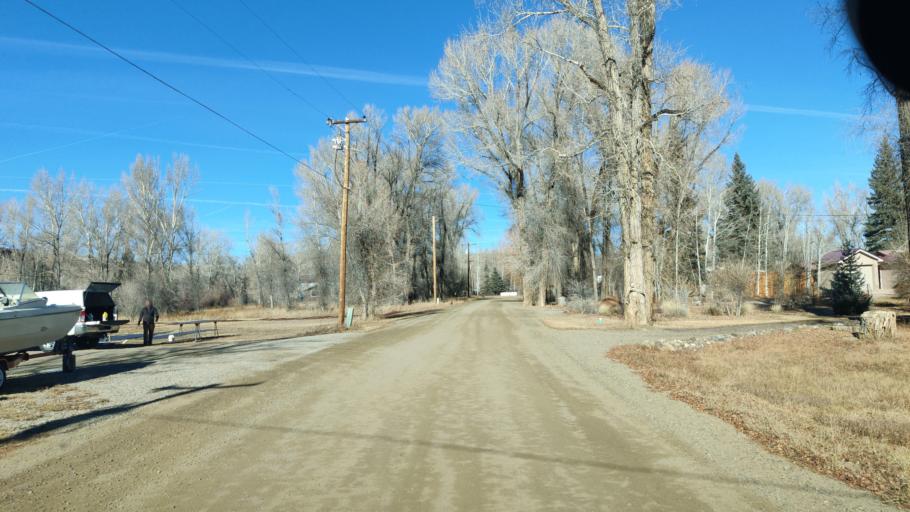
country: US
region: Colorado
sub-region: Gunnison County
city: Gunnison
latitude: 38.5357
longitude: -106.9500
